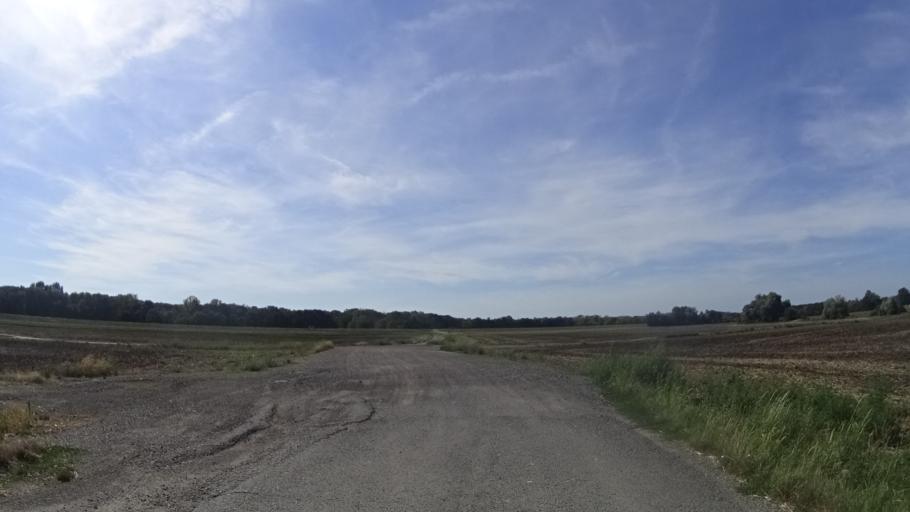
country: AT
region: Lower Austria
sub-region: Politischer Bezirk Ganserndorf
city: Durnkrut
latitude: 48.4241
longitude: 16.8664
